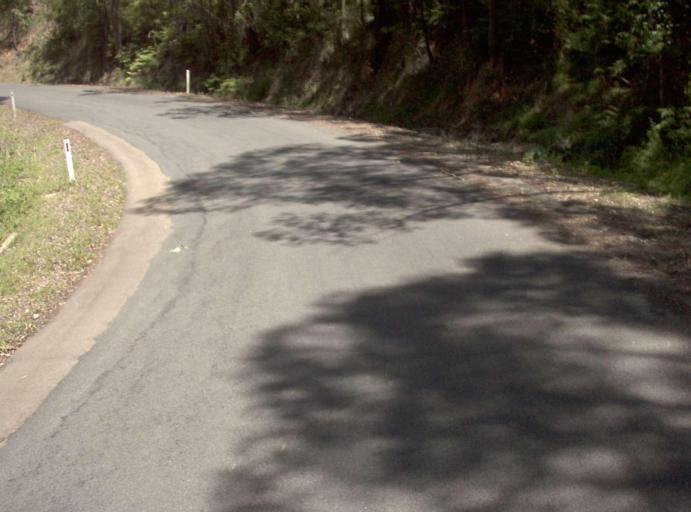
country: AU
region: New South Wales
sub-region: Bombala
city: Bombala
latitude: -37.4762
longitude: 148.9247
